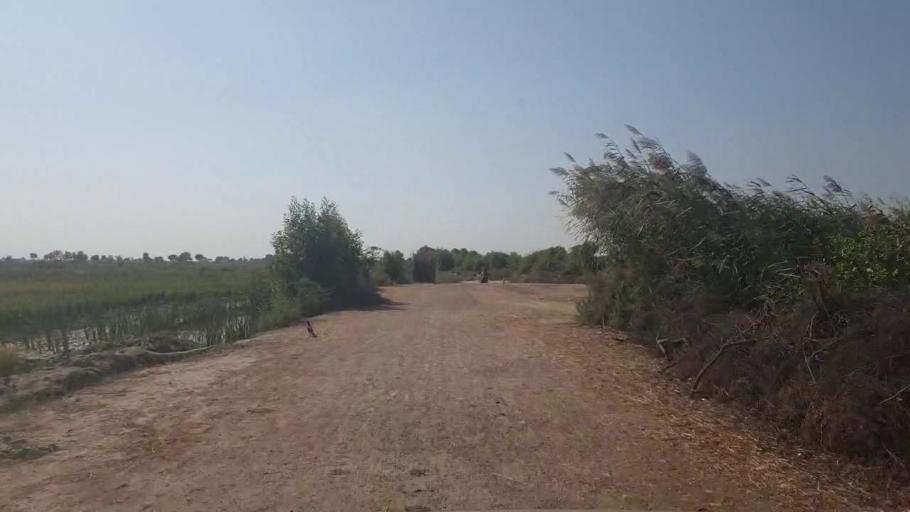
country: PK
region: Sindh
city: Badin
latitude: 24.5438
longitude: 68.8412
